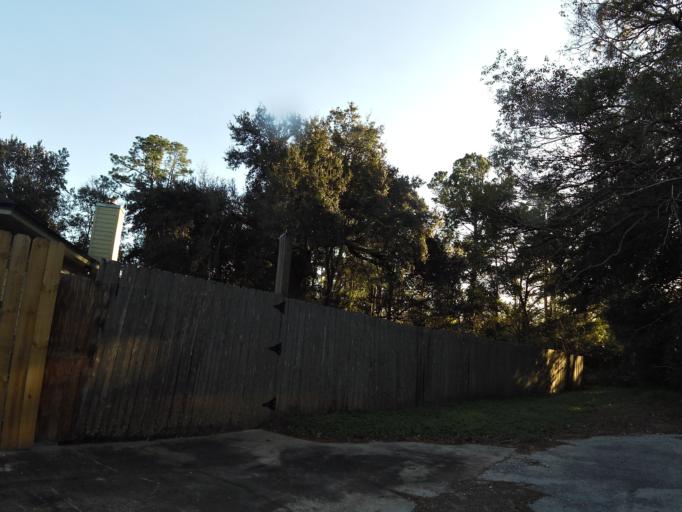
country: US
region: Florida
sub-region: Saint Johns County
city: Fruit Cove
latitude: 30.2100
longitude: -81.6056
